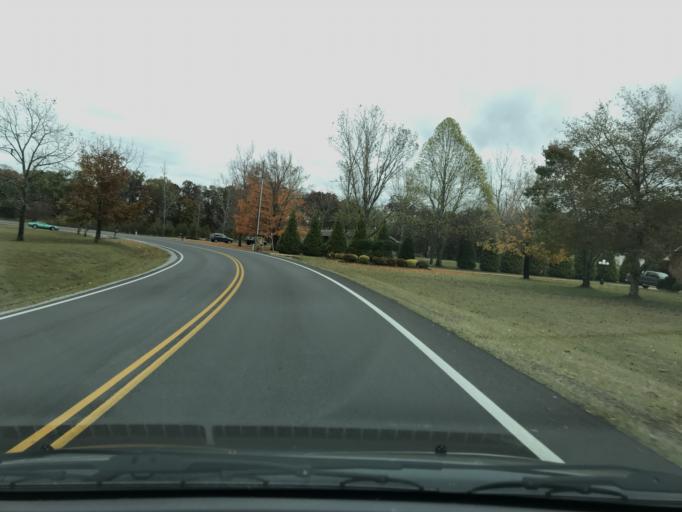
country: US
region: Tennessee
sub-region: Hamilton County
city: Collegedale
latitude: 35.1152
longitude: -85.0441
